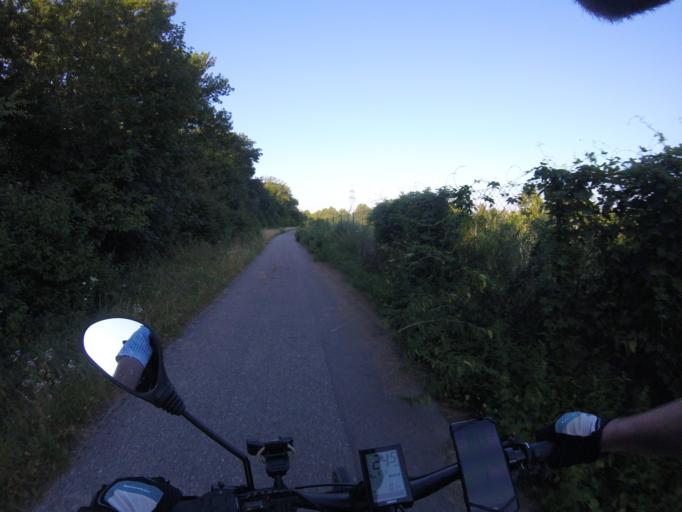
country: AT
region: Lower Austria
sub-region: Politischer Bezirk Baden
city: Ebreichsdorf
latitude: 47.9684
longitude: 16.3804
